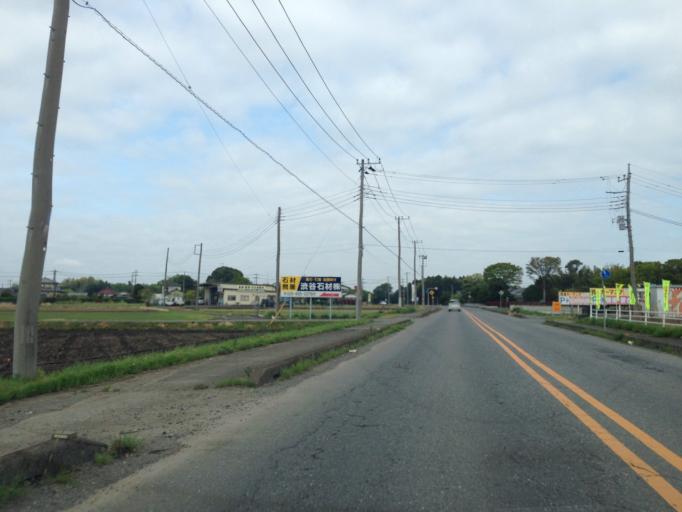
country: JP
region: Ibaraki
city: Ishige
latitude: 36.1454
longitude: 140.0283
